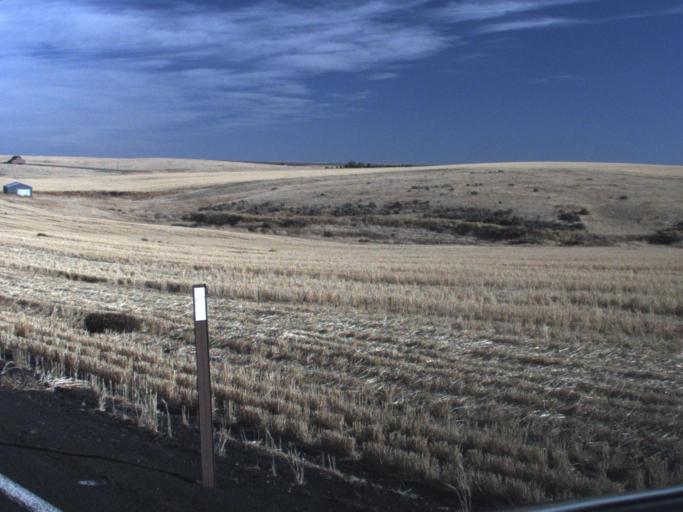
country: US
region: Washington
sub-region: Adams County
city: Ritzville
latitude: 47.2407
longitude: -118.6862
